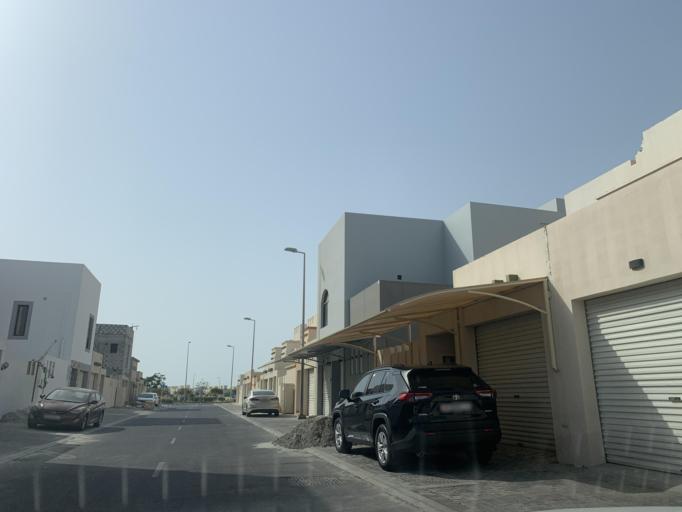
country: BH
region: Manama
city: Jidd Hafs
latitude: 26.2252
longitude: 50.4486
